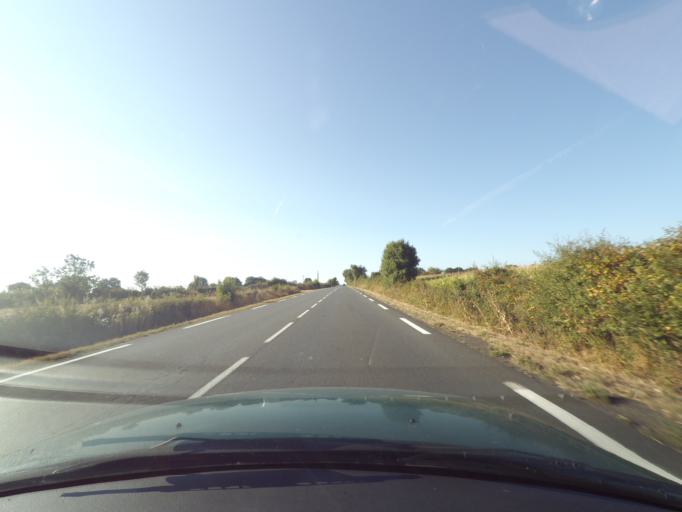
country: FR
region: Poitou-Charentes
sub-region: Departement des Deux-Sevres
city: Viennay
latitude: 46.7377
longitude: -0.3020
